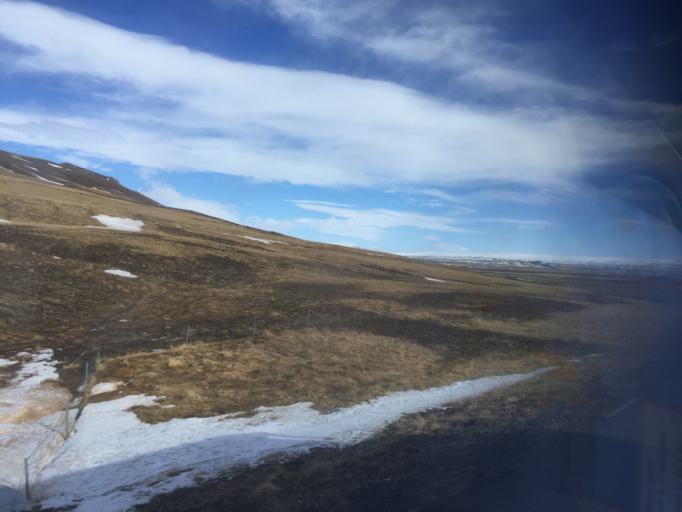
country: IS
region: South
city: Selfoss
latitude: 64.2710
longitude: -20.3841
